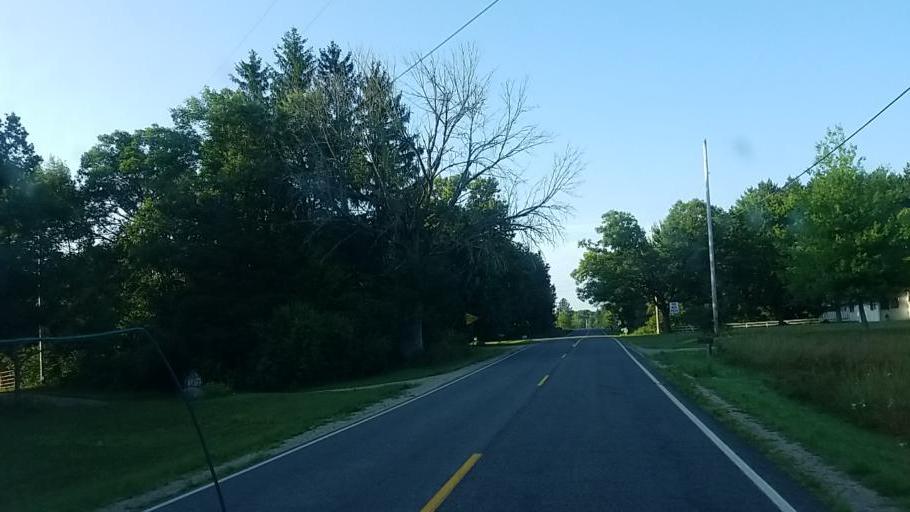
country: US
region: Michigan
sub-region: Montcalm County
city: Greenville
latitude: 43.2546
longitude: -85.3021
